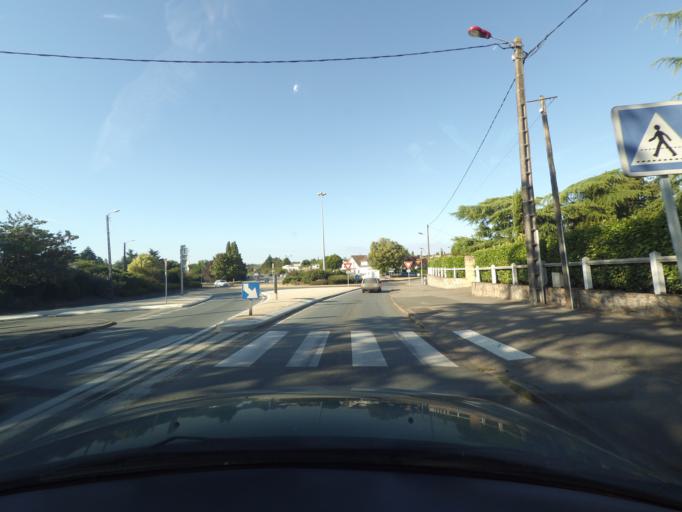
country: FR
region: Poitou-Charentes
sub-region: Departement des Deux-Sevres
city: Chatillon-sur-Thouet
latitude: 46.6631
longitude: -0.2383
